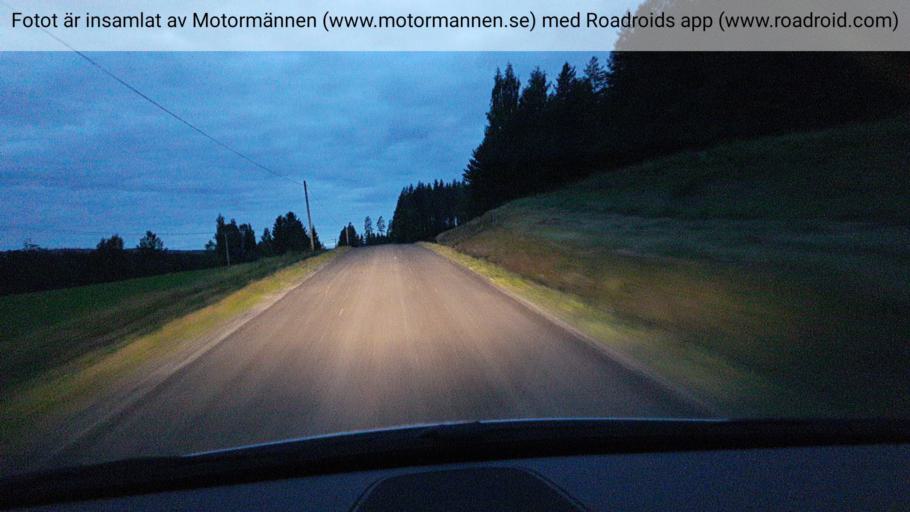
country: SE
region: Jaemtland
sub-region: Braecke Kommun
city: Braecke
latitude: 63.1967
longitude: 15.4742
